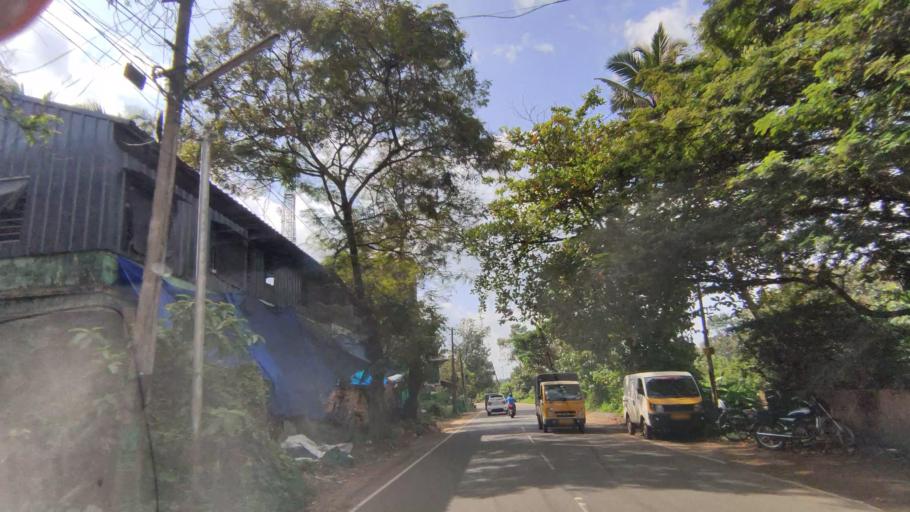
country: IN
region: Kerala
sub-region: Kottayam
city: Kottayam
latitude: 9.6712
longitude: 76.5547
